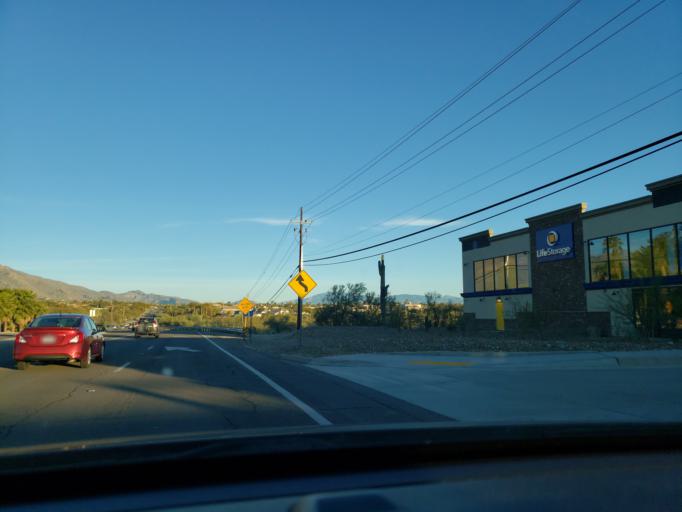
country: US
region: Arizona
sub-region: Pima County
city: Casas Adobes
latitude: 32.3226
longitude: -110.9726
